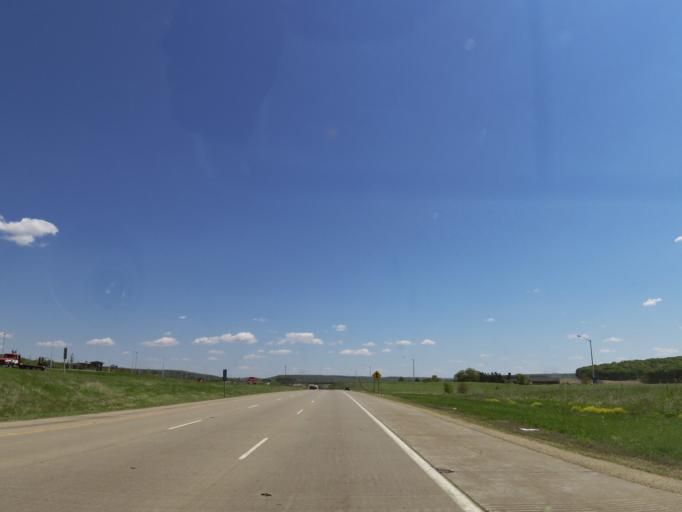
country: US
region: Wisconsin
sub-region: Columbia County
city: Poynette
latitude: 43.4272
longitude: -89.4801
